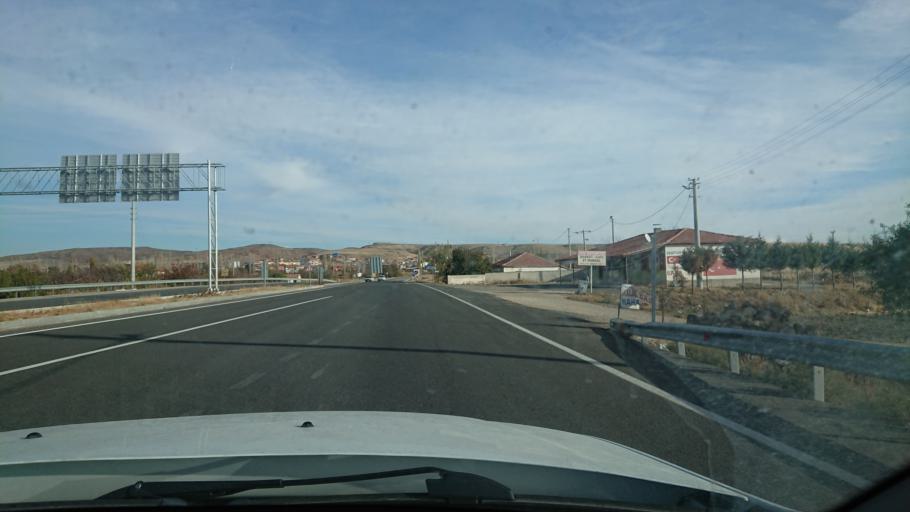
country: TR
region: Aksaray
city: Acipinar
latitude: 38.4790
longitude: 33.9013
